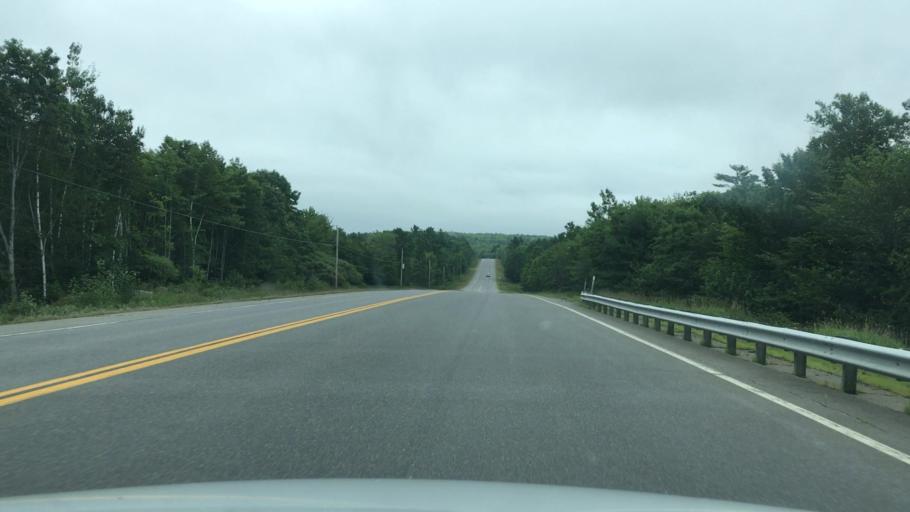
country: US
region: Maine
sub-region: Hancock County
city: Franklin
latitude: 44.8384
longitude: -68.1458
